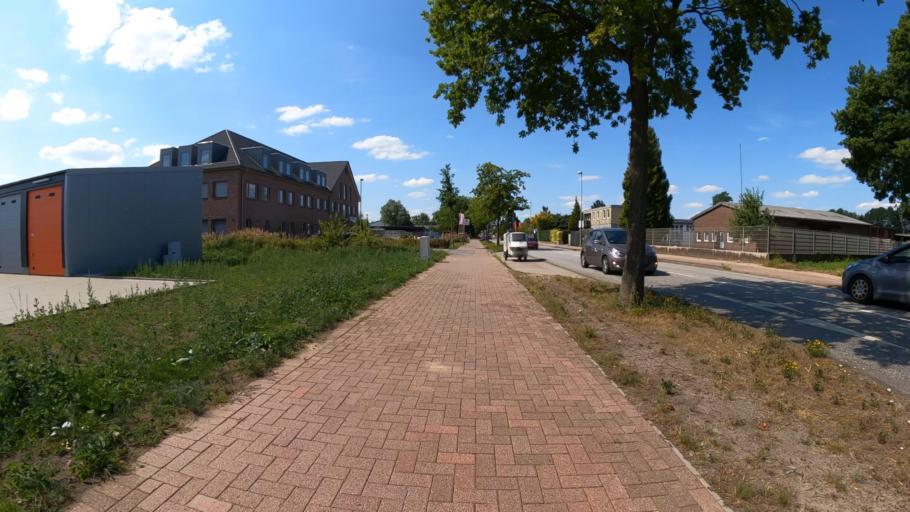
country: DE
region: Schleswig-Holstein
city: Kolln-Reisiek
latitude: 53.7415
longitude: 9.6930
